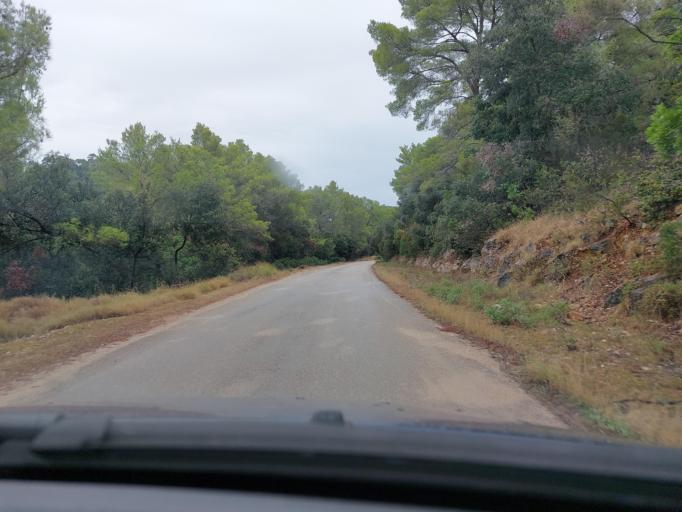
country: HR
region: Dubrovacko-Neretvanska
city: Smokvica
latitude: 42.7433
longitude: 16.8310
